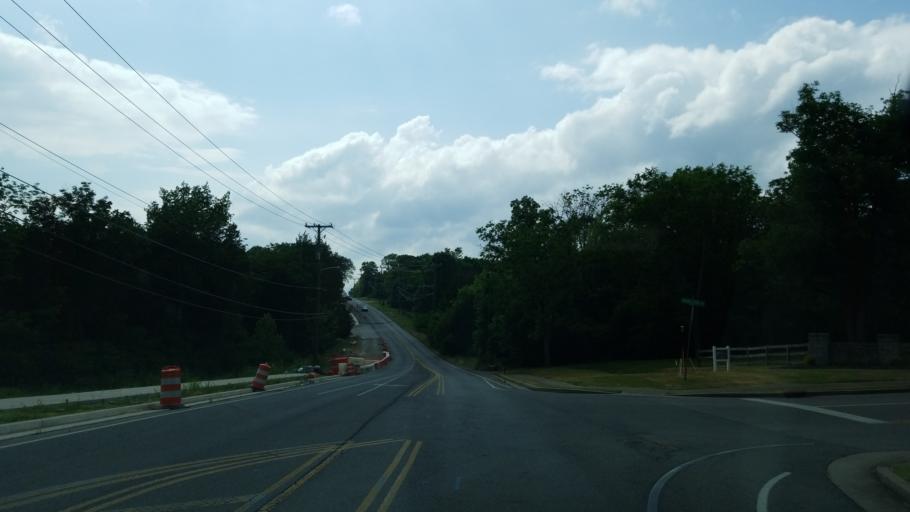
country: US
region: Tennessee
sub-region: Rutherford County
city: La Vergne
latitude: 36.0637
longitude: -86.6138
